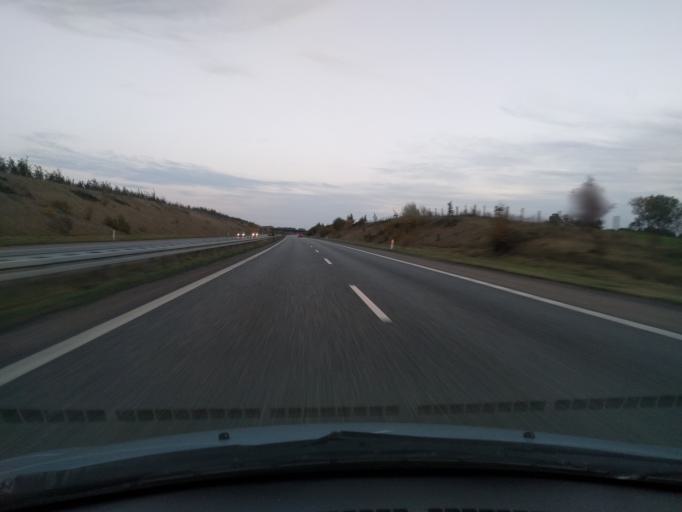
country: DK
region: South Denmark
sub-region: Faaborg-Midtfyn Kommune
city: Arslev
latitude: 55.2866
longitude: 10.4472
